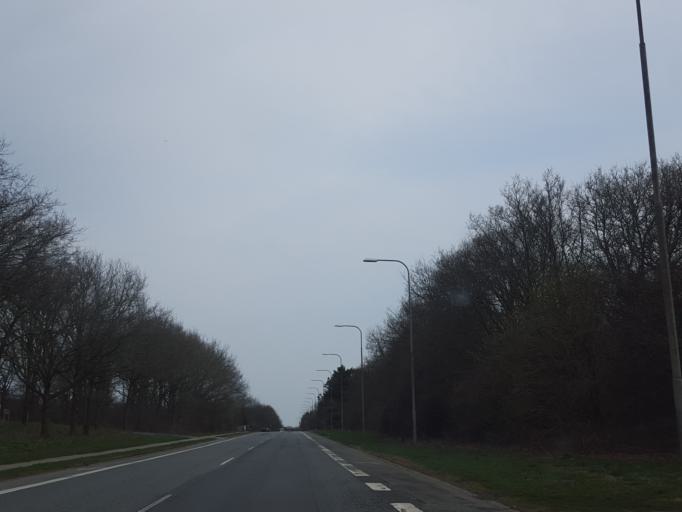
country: DK
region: South Denmark
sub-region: Esbjerg Kommune
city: Esbjerg
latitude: 55.4832
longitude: 8.4879
